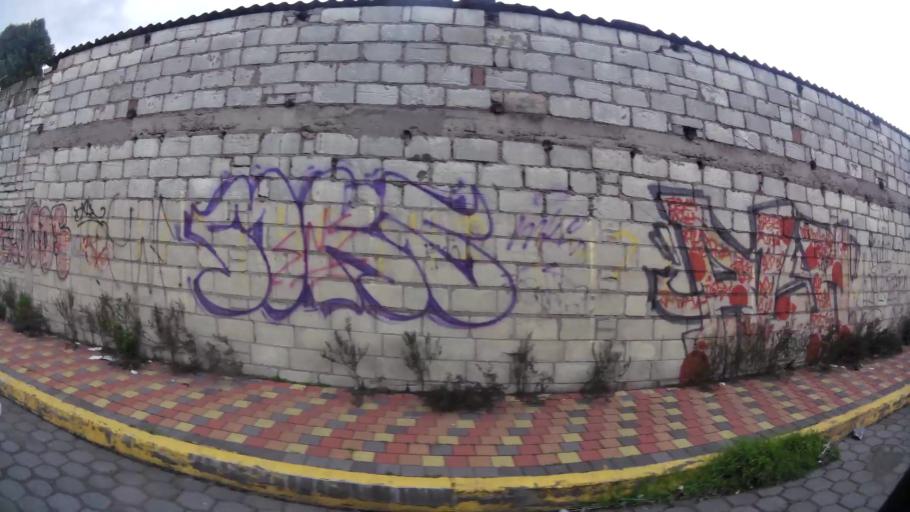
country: EC
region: Pichincha
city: Quito
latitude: -0.2826
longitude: -78.5361
